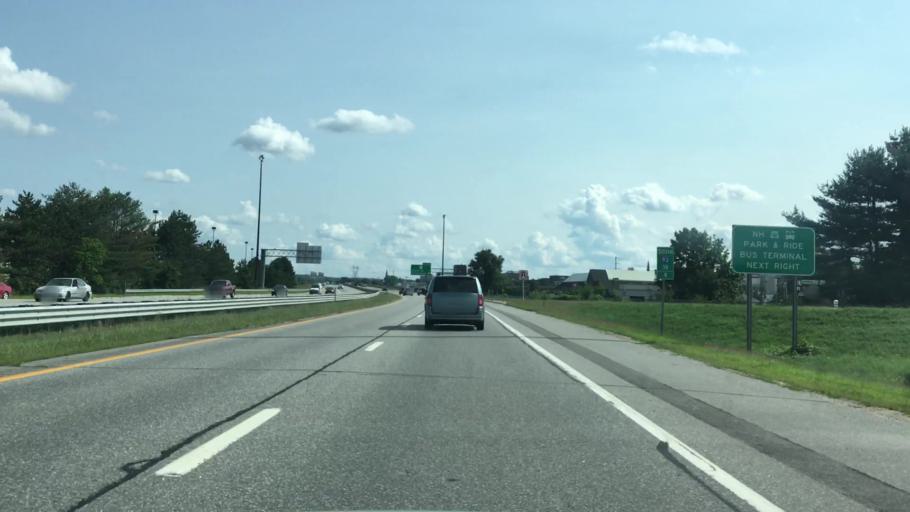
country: US
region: New Hampshire
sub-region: Merrimack County
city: Concord
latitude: 43.2144
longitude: -71.5340
